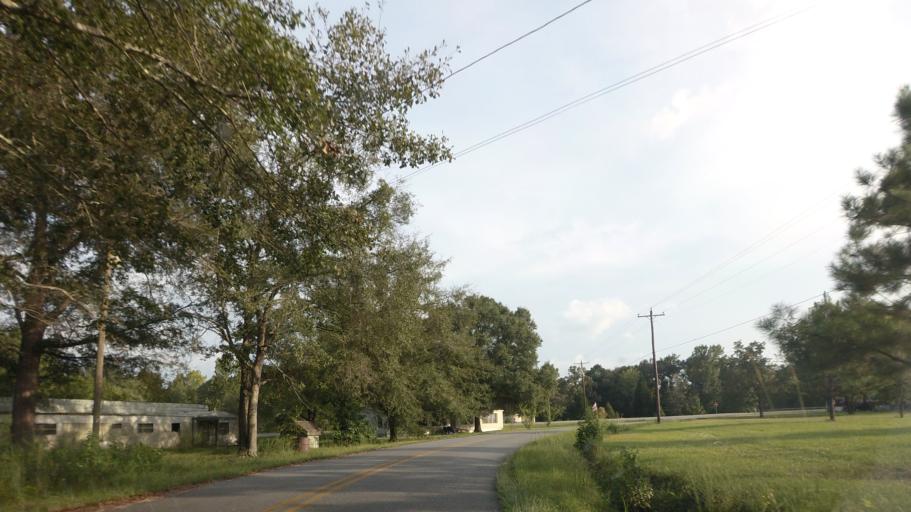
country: US
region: Georgia
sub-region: Wilkinson County
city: Gordon
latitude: 32.8261
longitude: -83.3905
